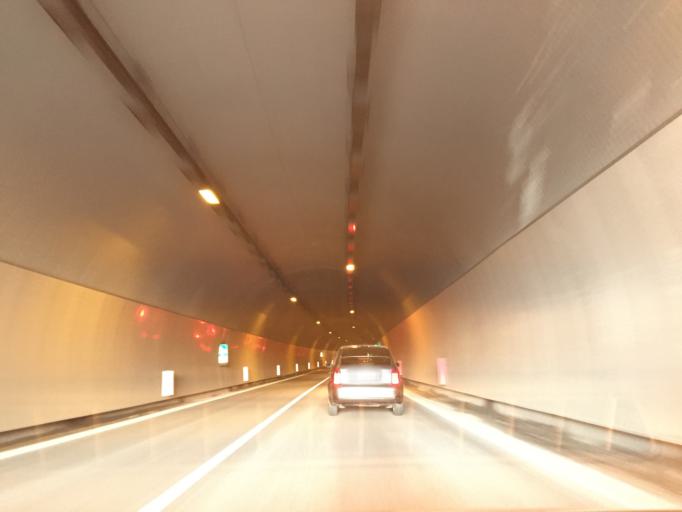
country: IT
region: Molise
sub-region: Provincia di Campobasso
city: Campobasso
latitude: 41.5546
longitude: 14.6554
